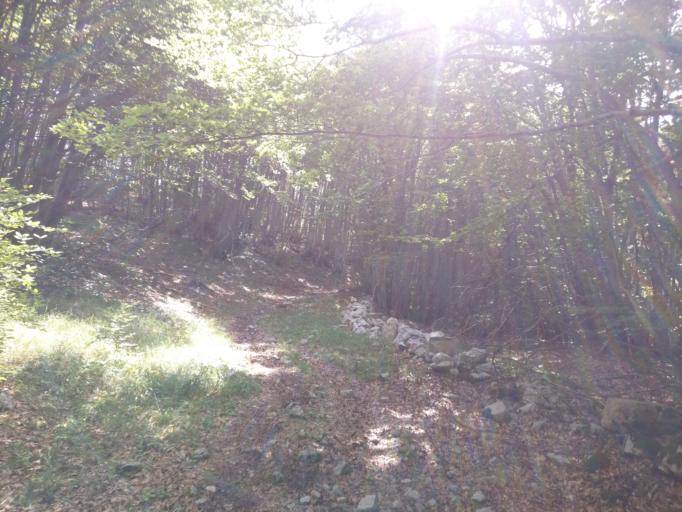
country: ME
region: Kotor
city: Kotor
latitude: 42.4084
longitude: 18.8399
